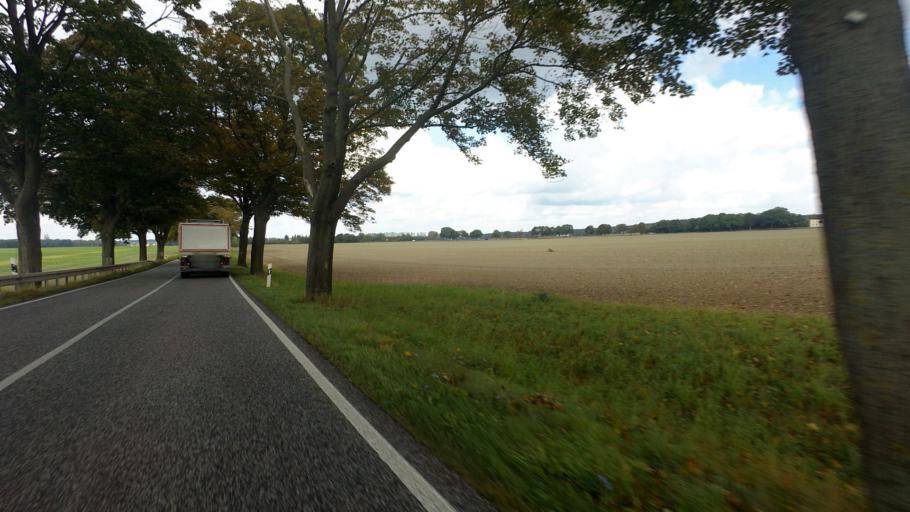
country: DE
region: Brandenburg
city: Juterbog
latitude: 51.9702
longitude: 13.1060
